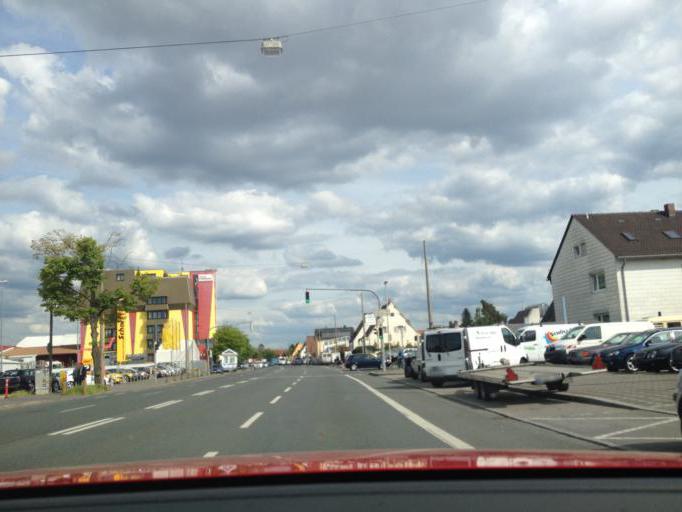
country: DE
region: Bavaria
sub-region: Regierungsbezirk Mittelfranken
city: Grossreuth bei Schweinau
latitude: 49.4517
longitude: 11.0263
